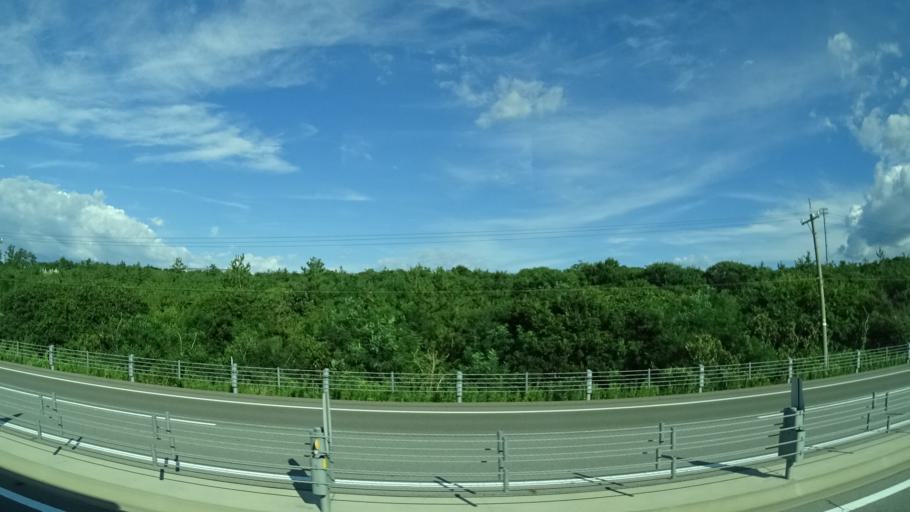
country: JP
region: Ishikawa
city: Kanazawa-shi
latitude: 36.6737
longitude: 136.6514
